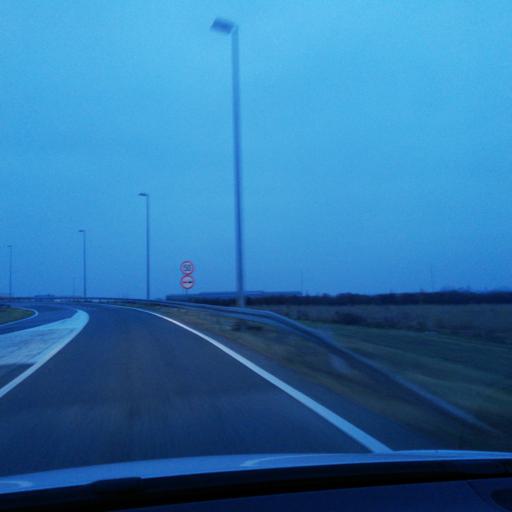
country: RS
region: Autonomna Pokrajina Vojvodina
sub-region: Sremski Okrug
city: Ruma
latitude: 44.9612
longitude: 19.8091
